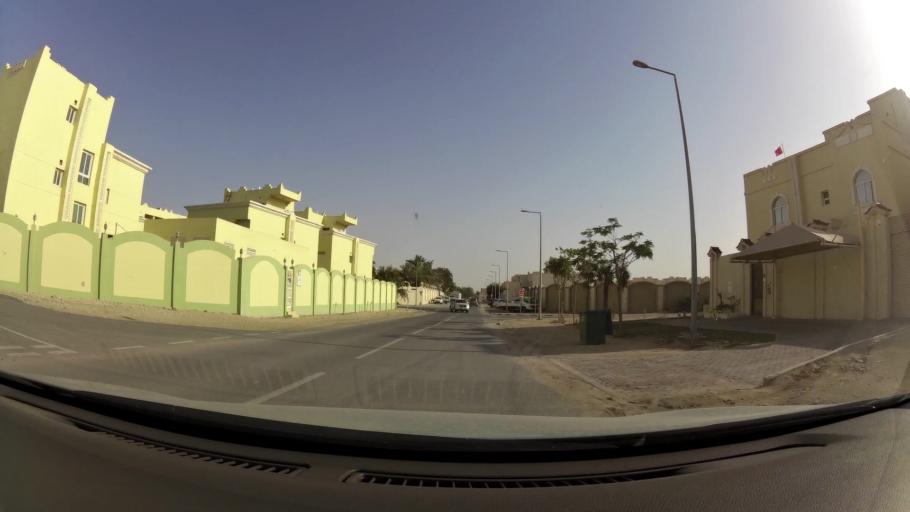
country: QA
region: Baladiyat ar Rayyan
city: Ar Rayyan
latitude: 25.3394
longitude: 51.4441
